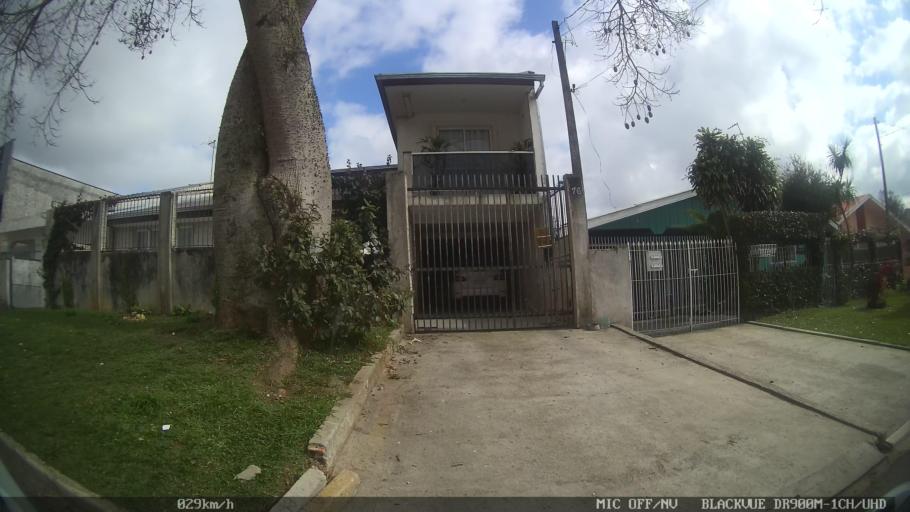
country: BR
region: Parana
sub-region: Almirante Tamandare
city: Almirante Tamandare
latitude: -25.3464
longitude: -49.2527
